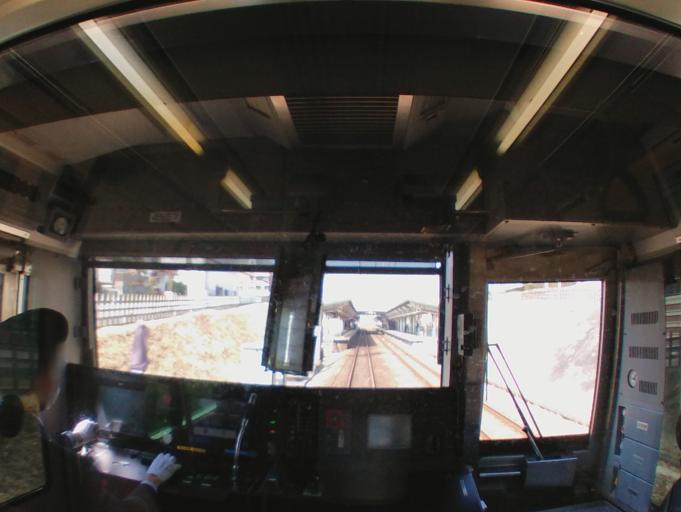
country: JP
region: Tokyo
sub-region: Machida-shi
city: Machida
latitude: 35.6034
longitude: 139.4856
